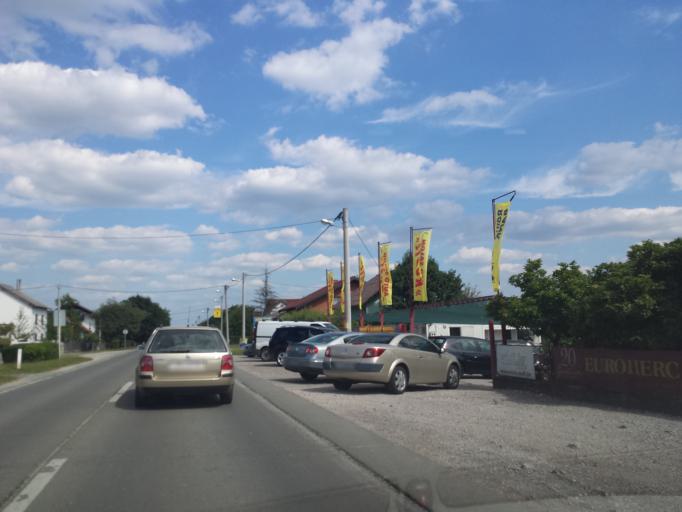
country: HR
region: Zagrebacka
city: Brckovljani
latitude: 45.8084
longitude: 16.2190
